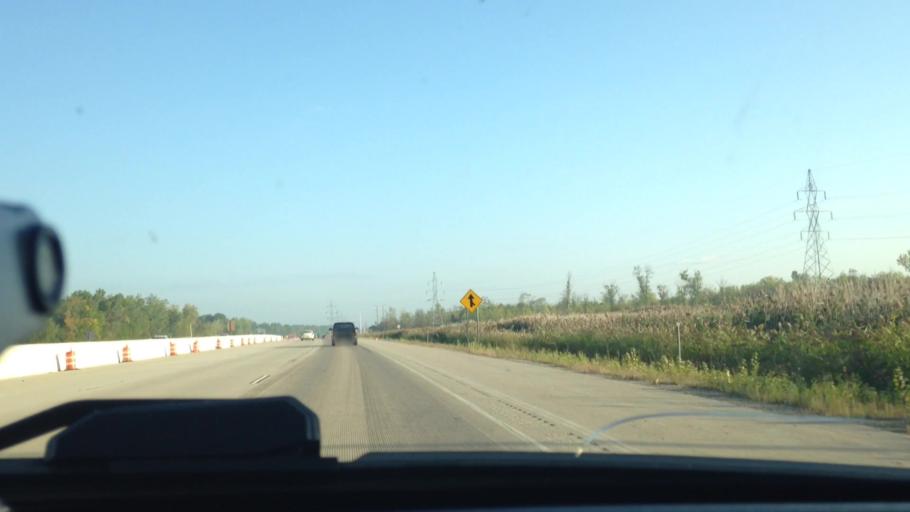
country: US
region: Wisconsin
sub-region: Brown County
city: Suamico
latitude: 44.5915
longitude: -88.0486
